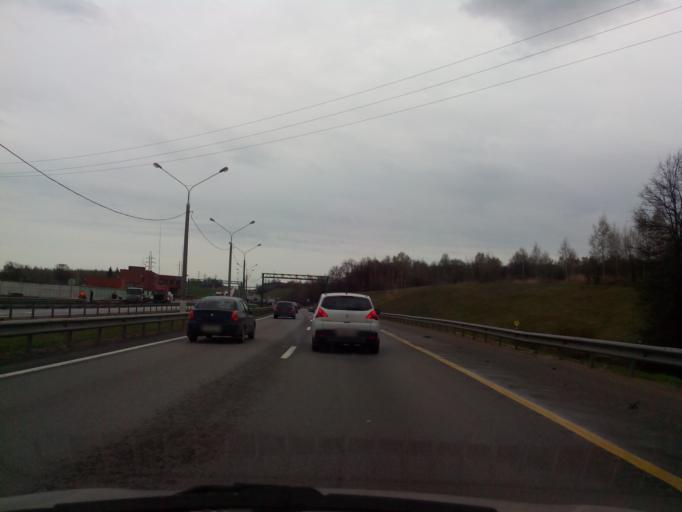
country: RU
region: Moskovskaya
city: Stupino
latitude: 54.8204
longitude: 38.0440
